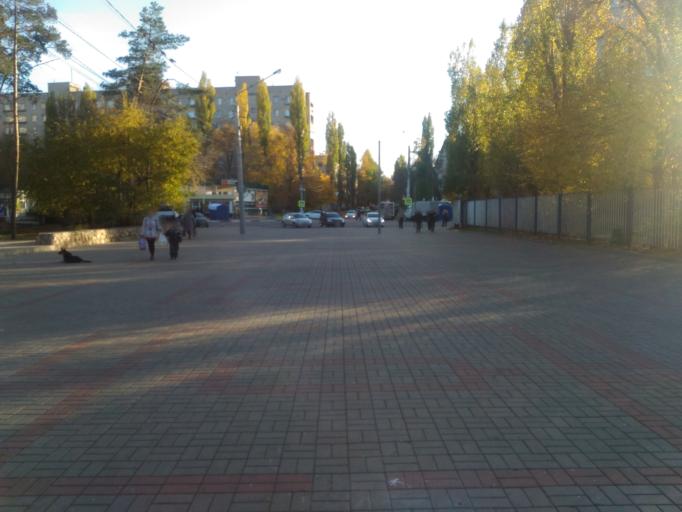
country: RU
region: Voronezj
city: Voronezh
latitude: 51.6522
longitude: 39.1283
